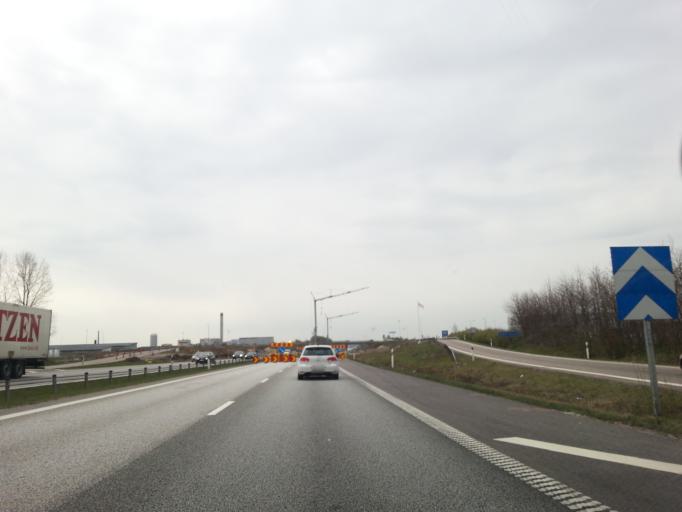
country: SE
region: Skane
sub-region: Angelholms Kommun
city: AEngelholm
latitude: 56.2544
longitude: 12.8980
